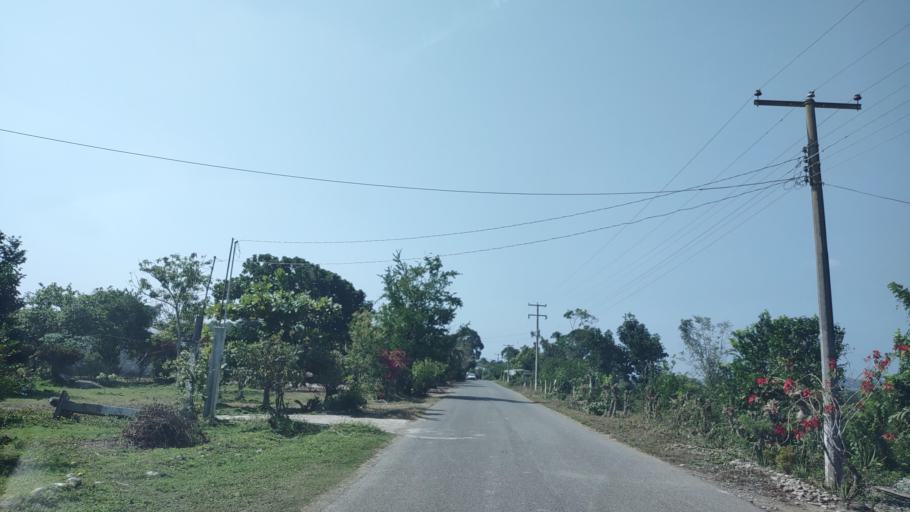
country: MX
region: Puebla
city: Espinal
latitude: 20.2568
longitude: -97.3246
